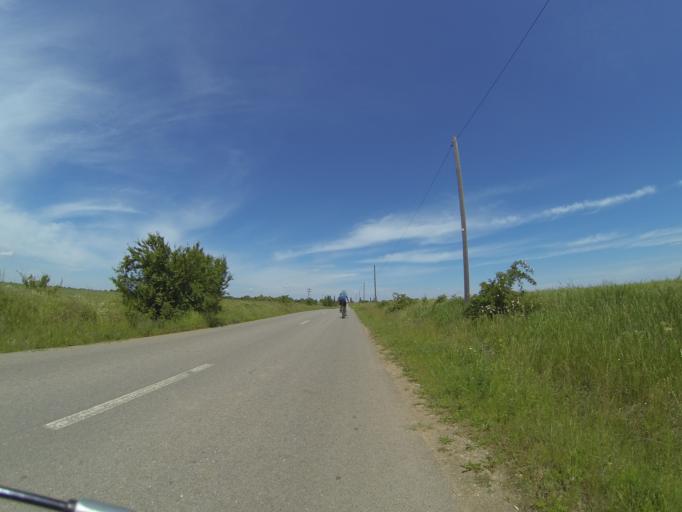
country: RO
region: Dolj
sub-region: Comuna Diosti
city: Radomir
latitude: 44.1497
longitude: 24.1636
